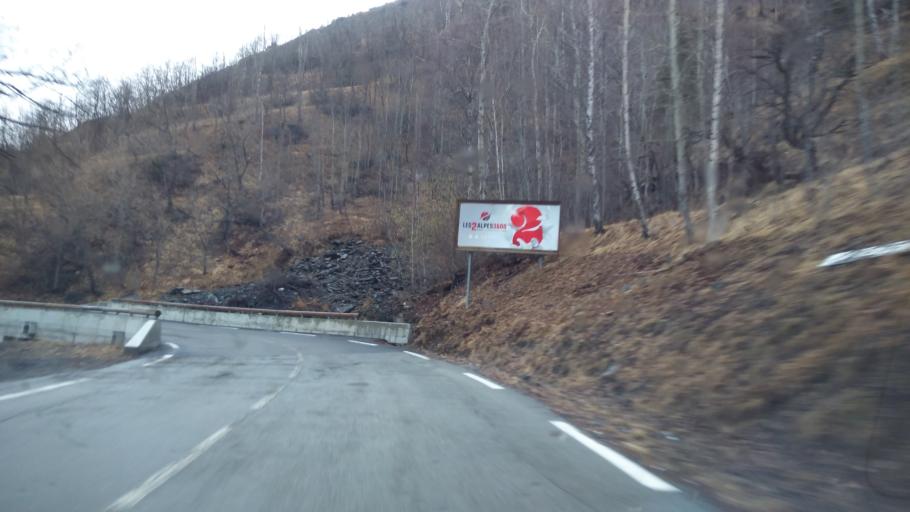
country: FR
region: Rhone-Alpes
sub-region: Departement de l'Isere
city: Mont-de-Lans
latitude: 45.0426
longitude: 6.1693
